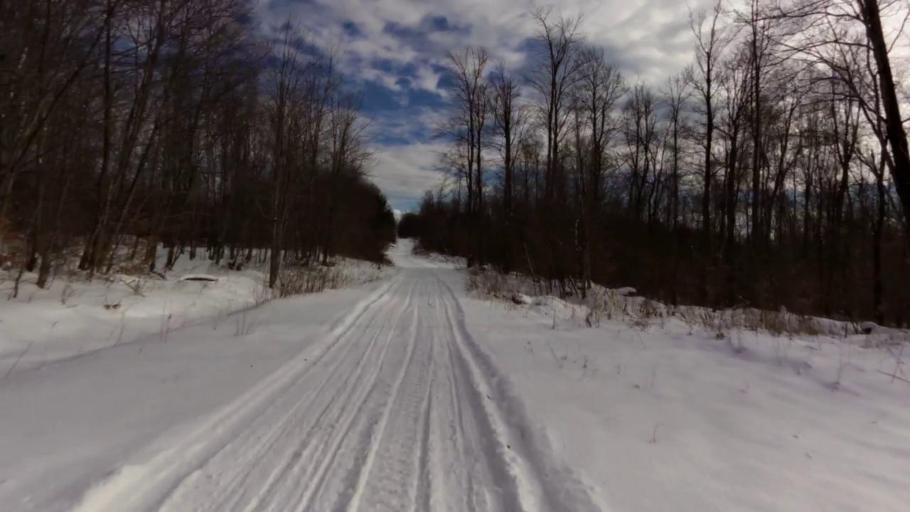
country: US
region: Pennsylvania
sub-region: McKean County
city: Foster Brook
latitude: 42.0163
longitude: -78.5488
